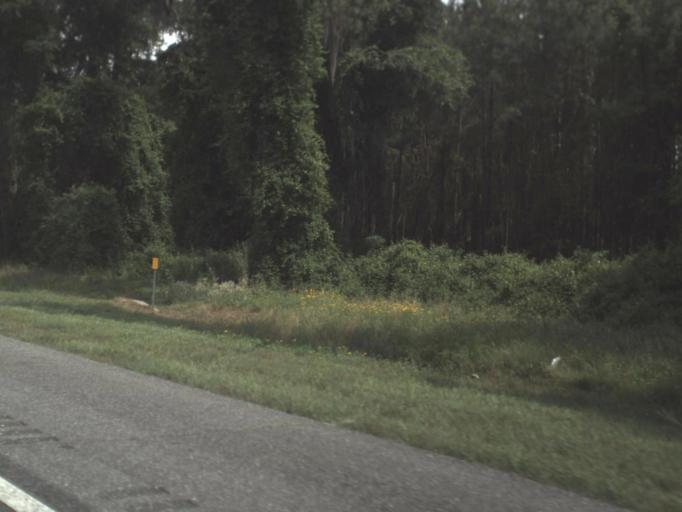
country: US
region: Florida
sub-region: Suwannee County
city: Live Oak
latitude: 30.2963
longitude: -82.8964
